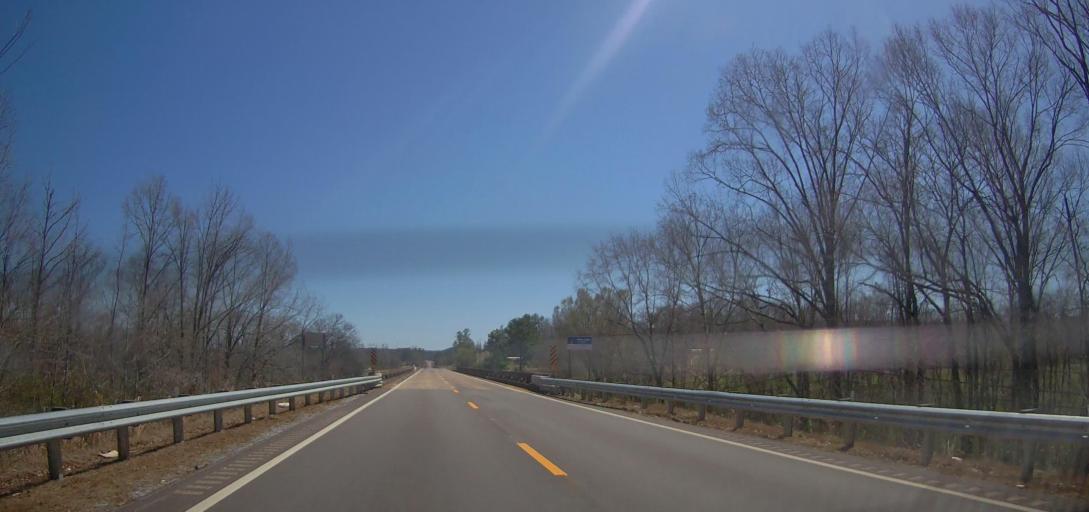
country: US
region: Alabama
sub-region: Calhoun County
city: Ohatchee
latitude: 33.7794
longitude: -86.0019
